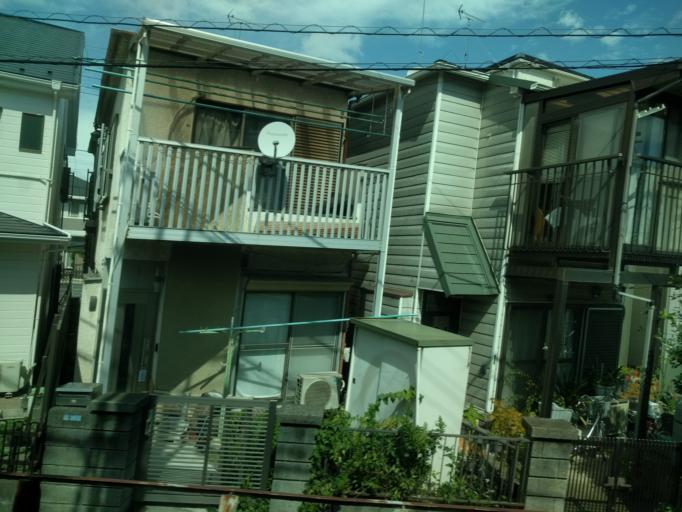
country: JP
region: Tokyo
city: Chofugaoka
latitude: 35.6151
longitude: 139.5805
